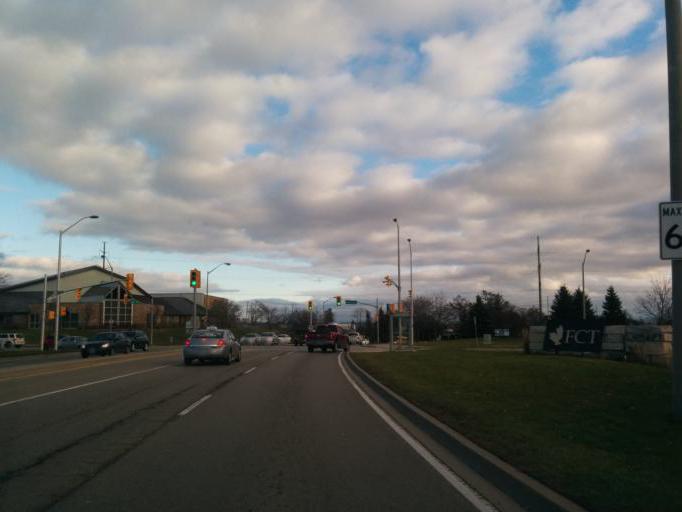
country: CA
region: Ontario
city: Oakville
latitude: 43.4914
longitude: -79.6567
